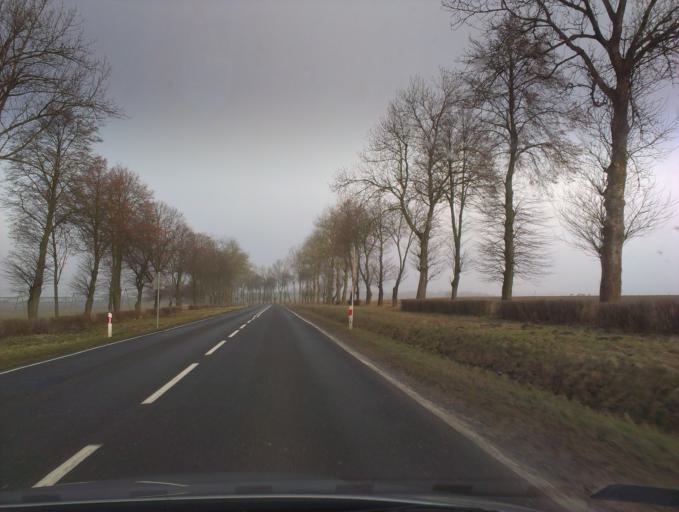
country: PL
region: West Pomeranian Voivodeship
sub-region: Koszalin
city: Koszalin
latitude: 54.1506
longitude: 16.2430
